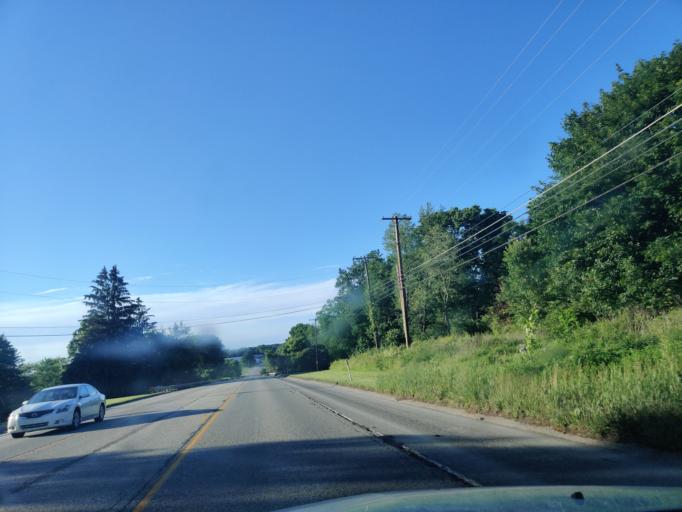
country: US
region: Pennsylvania
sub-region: Lawrence County
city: New Castle Northwest
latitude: 41.0721
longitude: -80.3615
